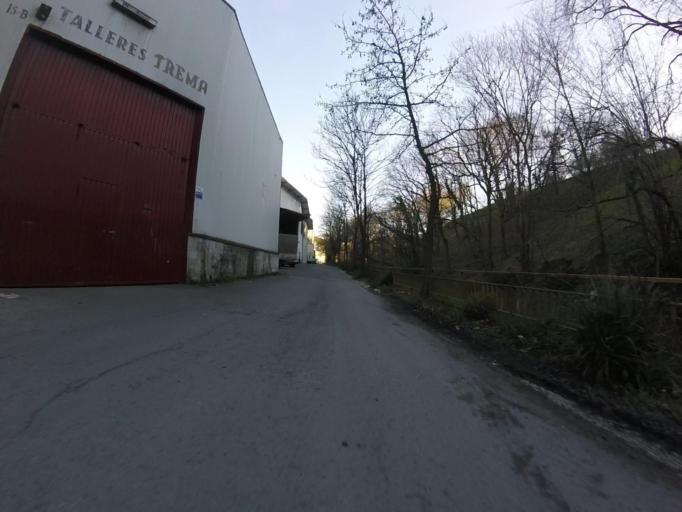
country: ES
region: Basque Country
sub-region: Provincia de Guipuzcoa
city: Errenteria
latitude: 43.2987
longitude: -1.8842
